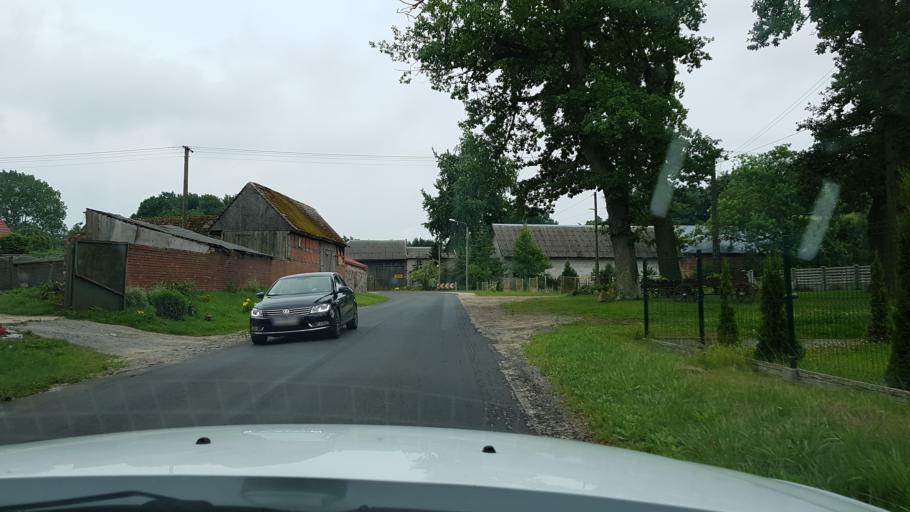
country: PL
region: West Pomeranian Voivodeship
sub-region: Powiat slawienski
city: Slawno
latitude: 54.4888
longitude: 16.5819
